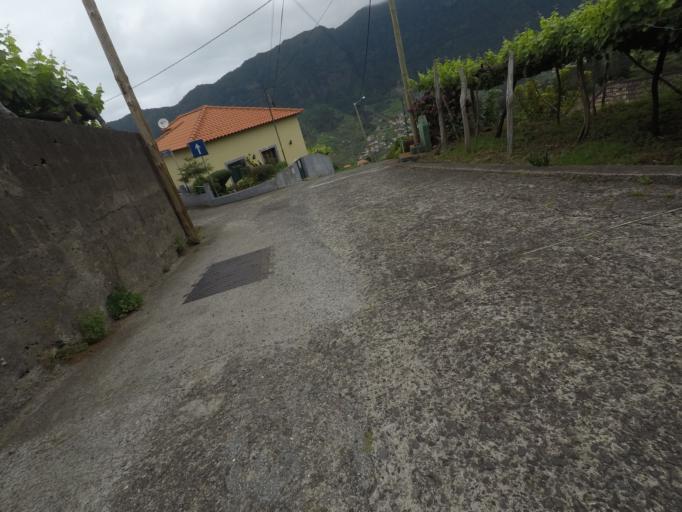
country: PT
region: Madeira
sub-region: Sao Vicente
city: Sao Vicente
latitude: 32.7819
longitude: -17.0426
